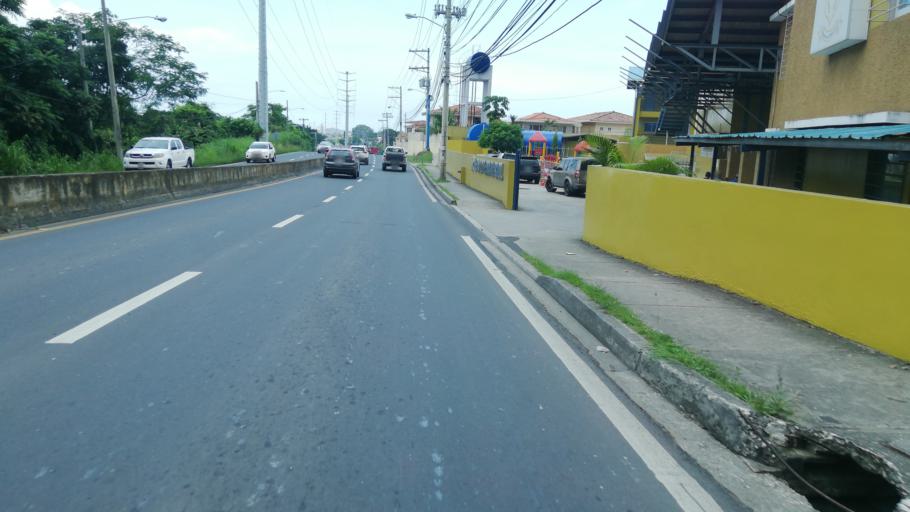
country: PA
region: Panama
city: San Miguelito
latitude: 9.0602
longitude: -79.4622
